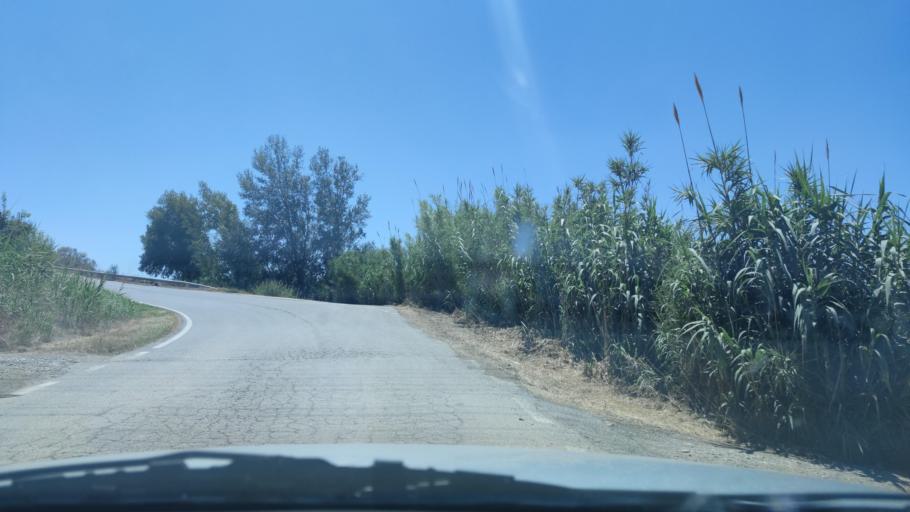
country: ES
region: Catalonia
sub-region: Provincia de Lleida
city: Alcoletge
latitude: 41.6551
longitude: 0.6686
